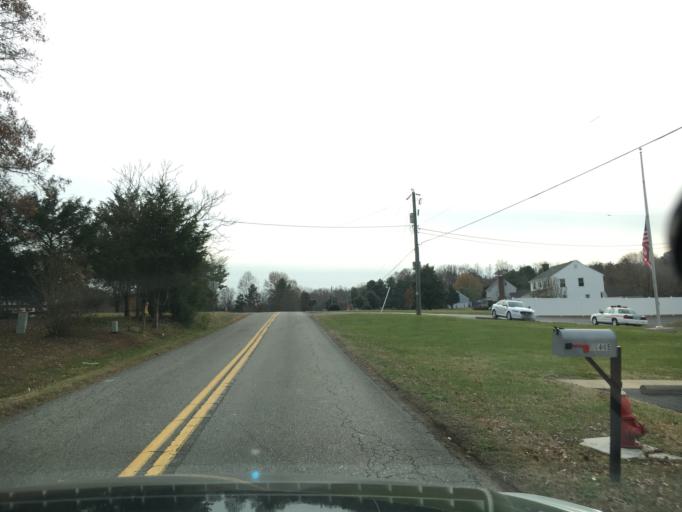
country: US
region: Virginia
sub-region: Henrico County
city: Wyndham
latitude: 37.7248
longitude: -77.6791
